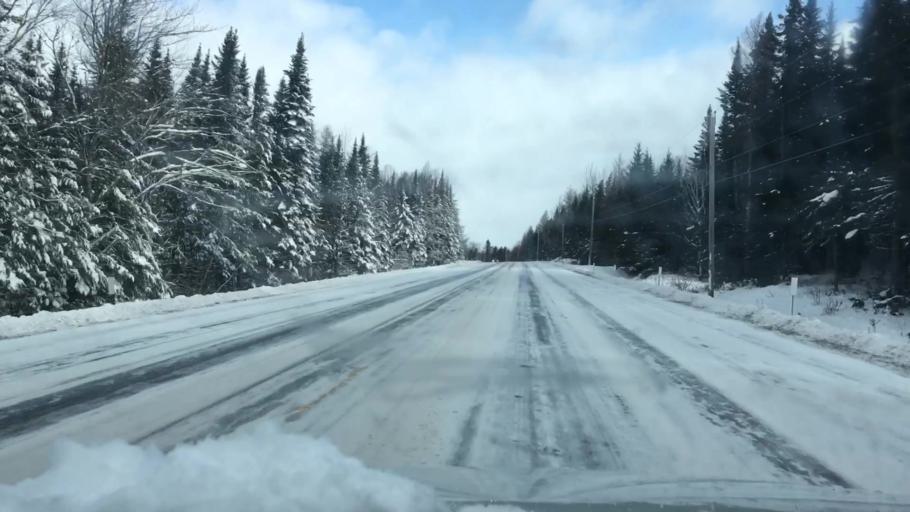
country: US
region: Maine
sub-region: Aroostook County
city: Van Buren
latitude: 47.0642
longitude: -67.9891
